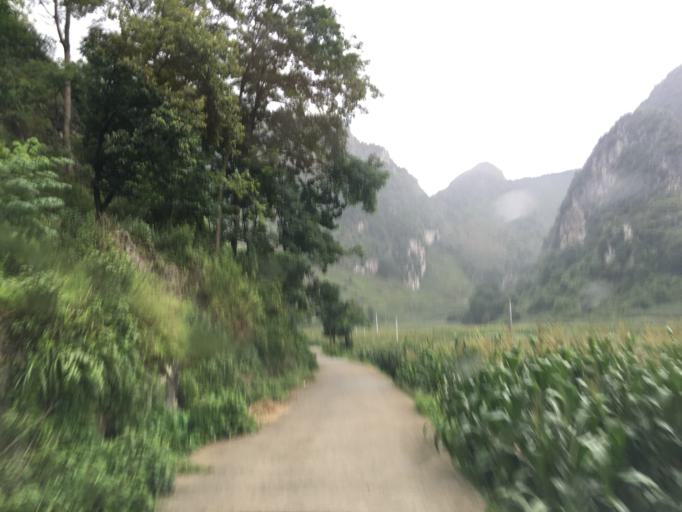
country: CN
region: Guangxi Zhuangzu Zizhiqu
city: Xinzhou
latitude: 24.9909
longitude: 105.6402
